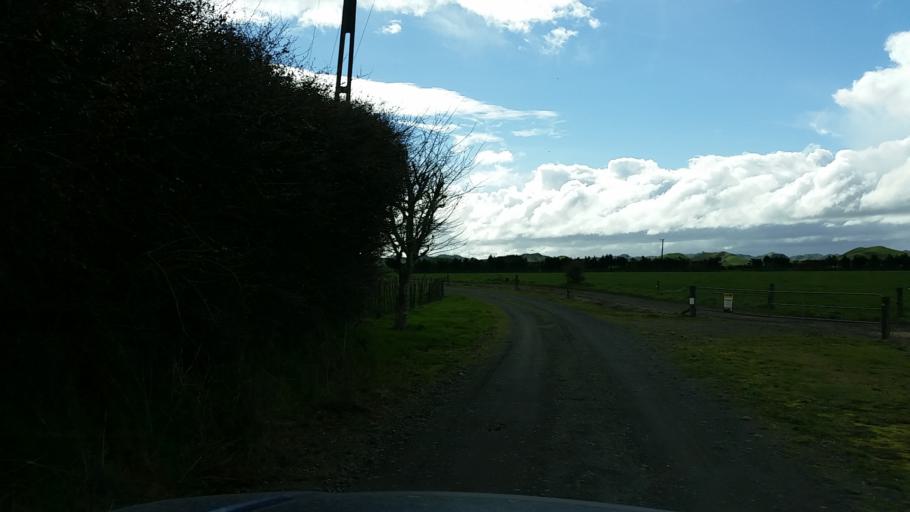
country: NZ
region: Taranaki
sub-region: South Taranaki District
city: Eltham
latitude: -39.3511
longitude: 174.3840
